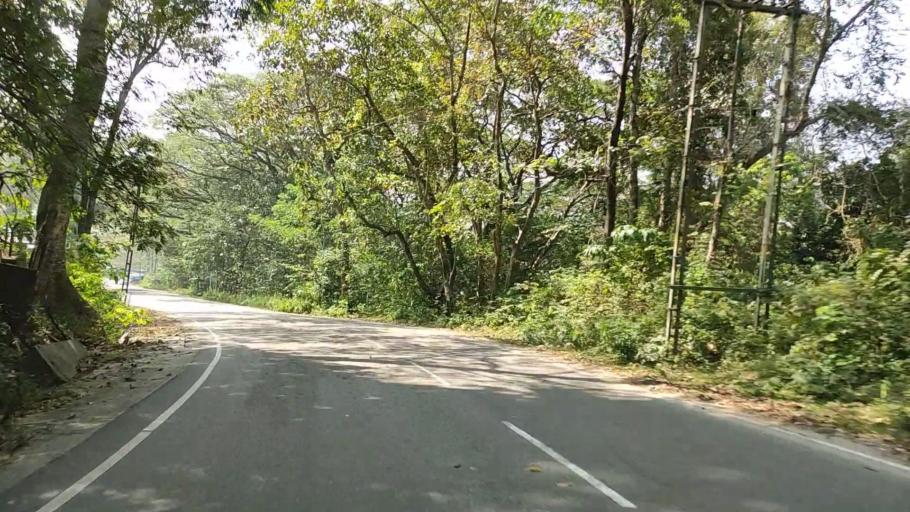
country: IN
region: Kerala
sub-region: Kollam
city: Punalur
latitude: 8.9588
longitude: 77.0664
